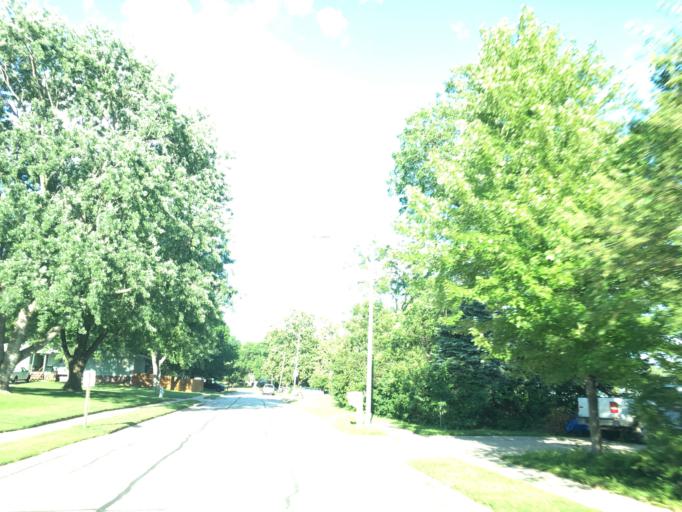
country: US
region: Nebraska
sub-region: Sarpy County
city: La Vista
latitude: 41.1743
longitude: -95.9900
